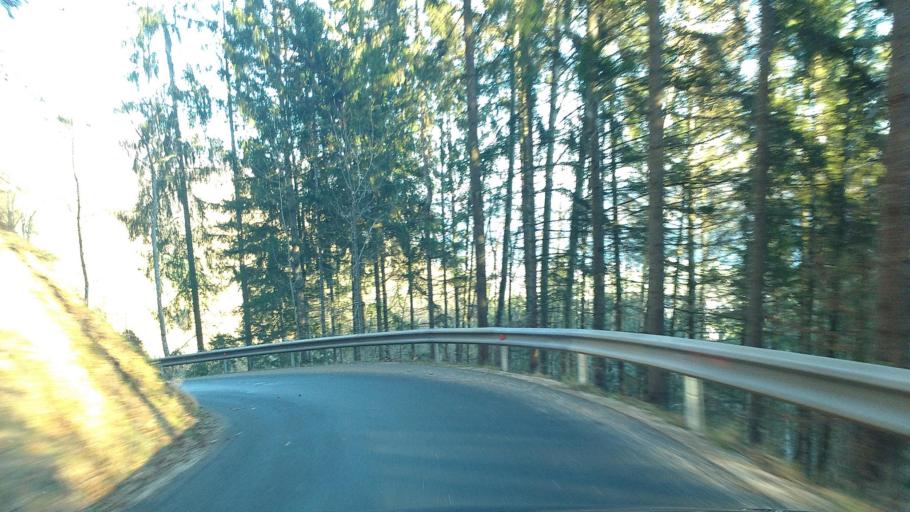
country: AT
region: Upper Austria
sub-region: Politischer Bezirk Kirchdorf an der Krems
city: Micheldorf in Oberoesterreich
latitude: 47.8940
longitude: 14.2189
